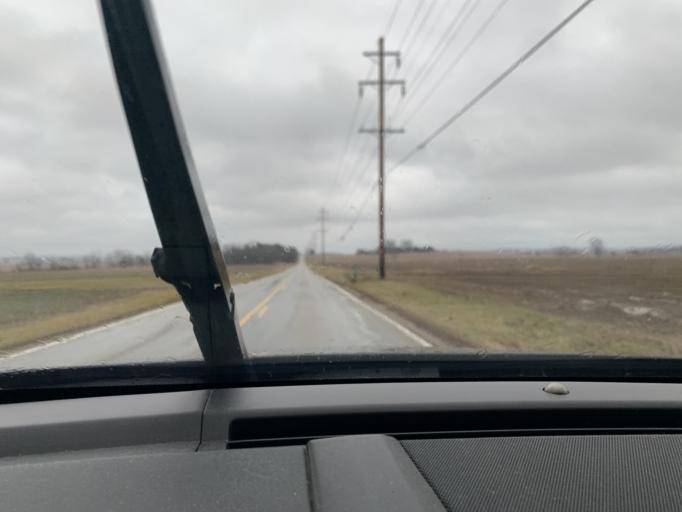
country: US
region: Ohio
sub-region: Ross County
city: Kingston
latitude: 39.4755
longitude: -82.8934
